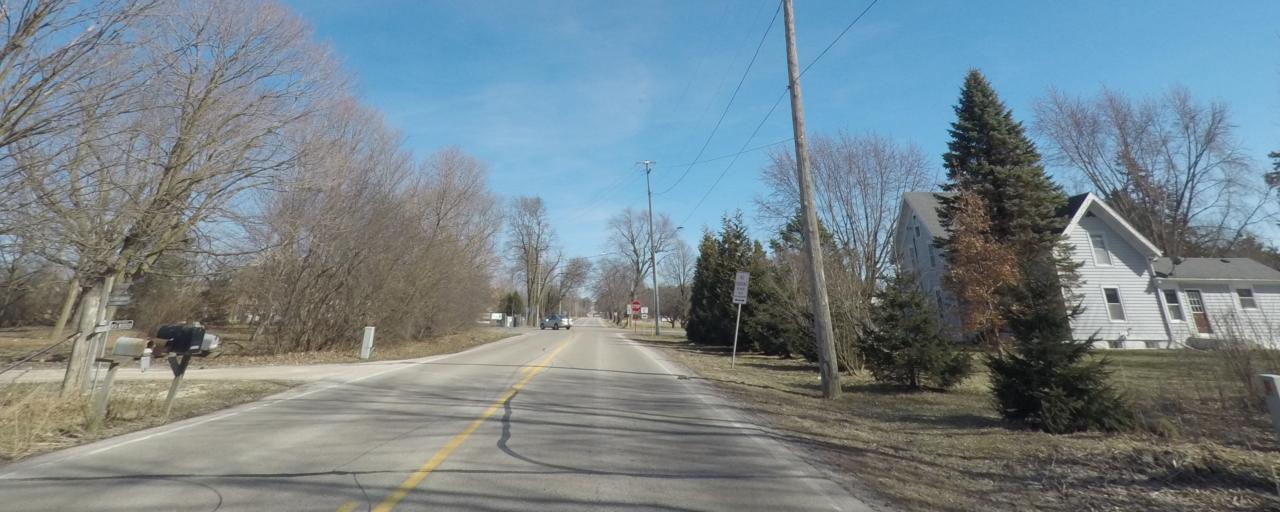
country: US
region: Wisconsin
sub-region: Waukesha County
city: Hartland
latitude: 43.1198
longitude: -88.3438
